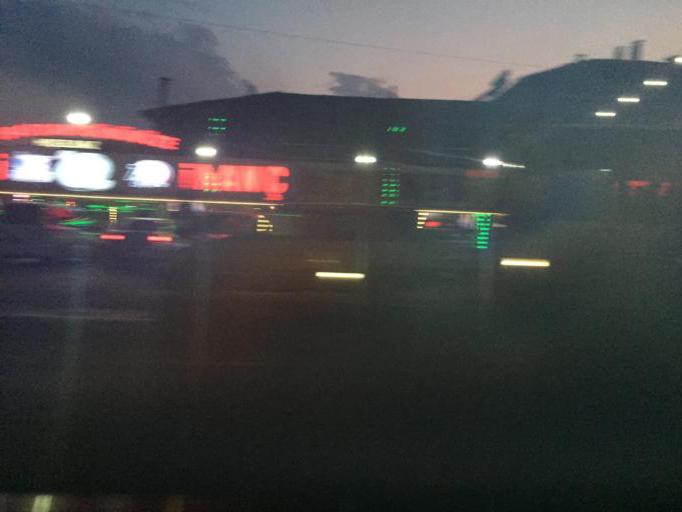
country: TR
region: Samsun
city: Kavak
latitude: 41.1379
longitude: 36.1240
